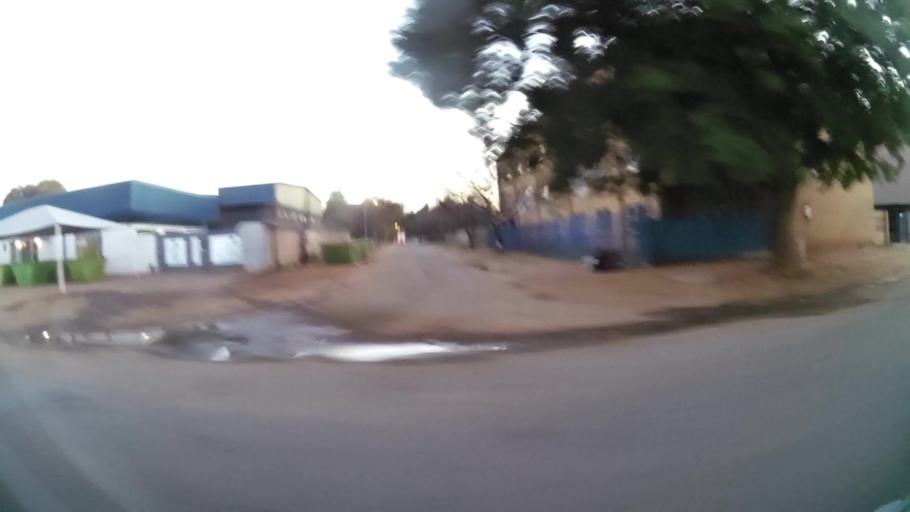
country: ZA
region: North-West
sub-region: Bojanala Platinum District Municipality
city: Rustenburg
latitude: -25.6680
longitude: 27.2513
